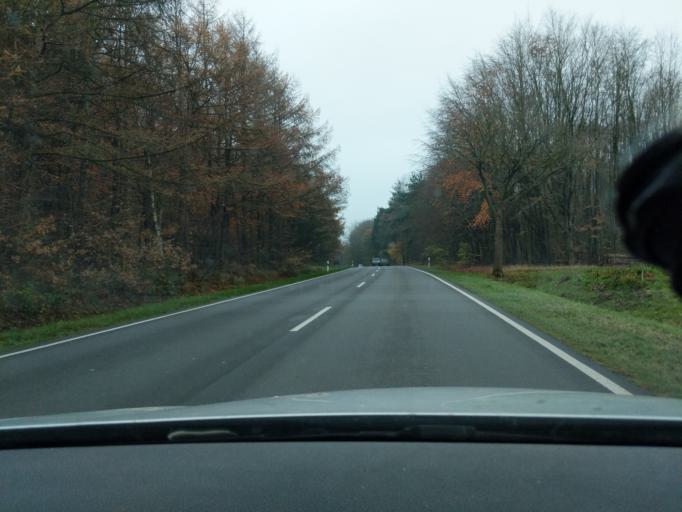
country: DE
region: Lower Saxony
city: Zeven
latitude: 53.2472
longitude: 9.2748
